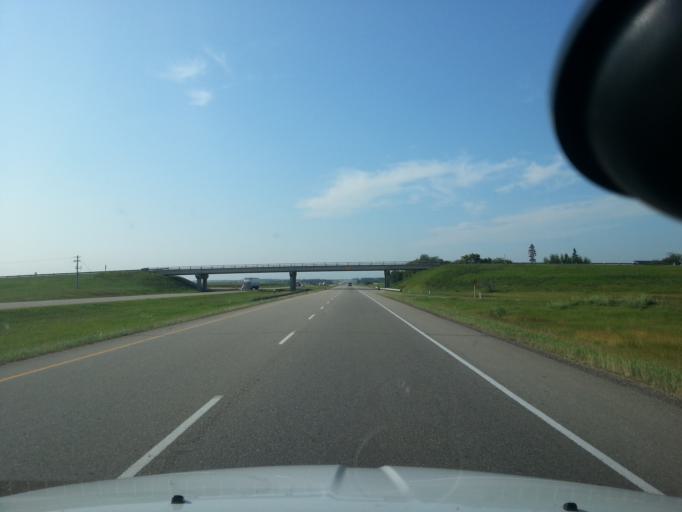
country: CA
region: Alberta
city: Ponoka
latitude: 52.7871
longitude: -113.6441
